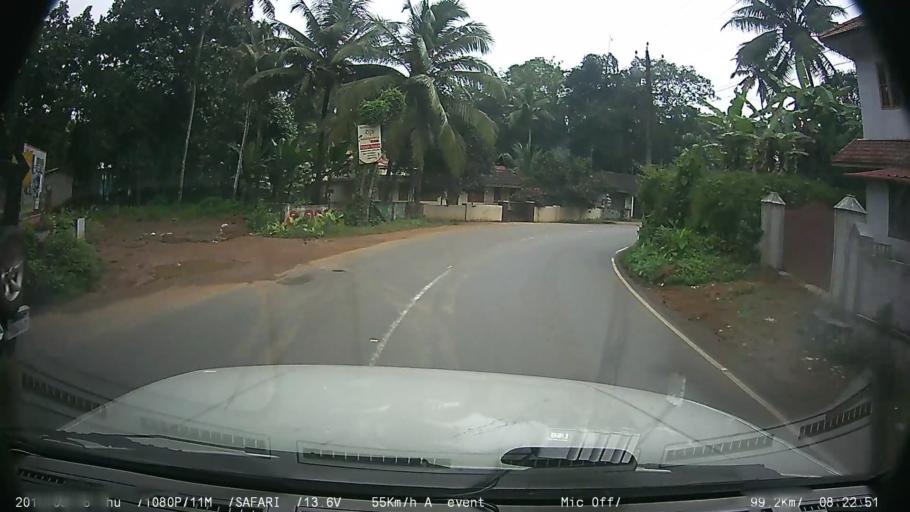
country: IN
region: Kerala
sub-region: Kottayam
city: Palackattumala
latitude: 9.6655
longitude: 76.6087
